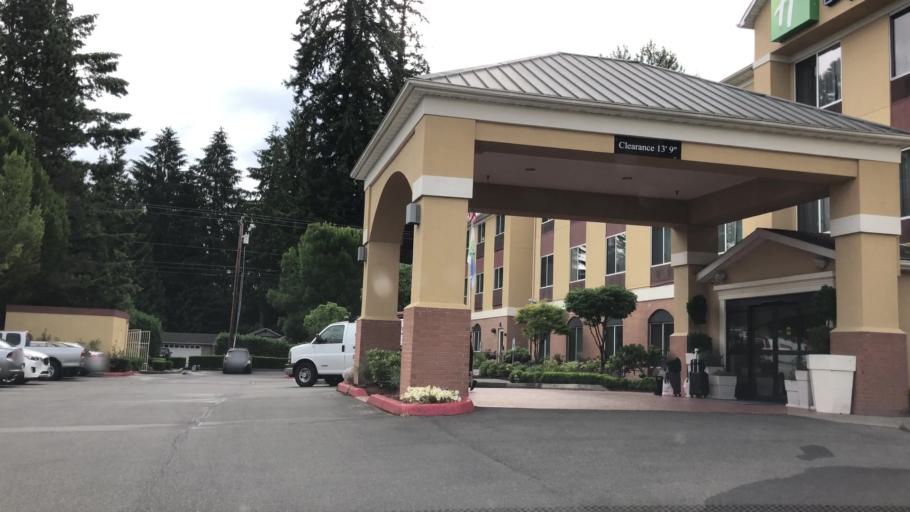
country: US
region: Washington
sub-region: King County
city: Bothell
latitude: 47.7898
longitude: -122.2141
